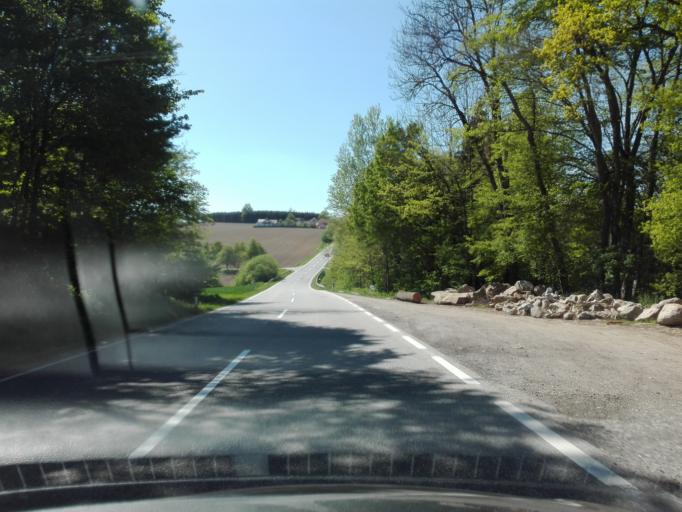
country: AT
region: Upper Austria
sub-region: Politischer Bezirk Grieskirchen
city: Bad Schallerbach
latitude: 48.3212
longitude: 13.8877
